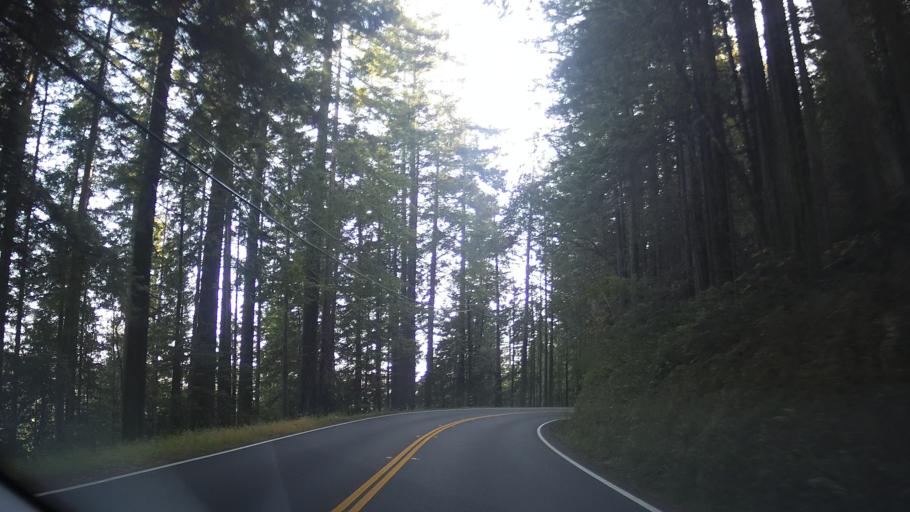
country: US
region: California
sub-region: Mendocino County
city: Fort Bragg
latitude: 39.4074
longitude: -123.7286
